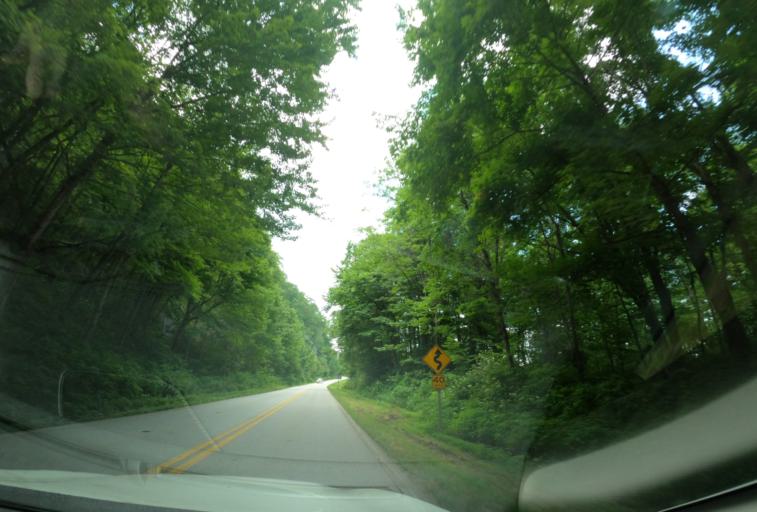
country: US
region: South Carolina
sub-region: Oconee County
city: Walhalla
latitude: 35.0294
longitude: -83.0175
